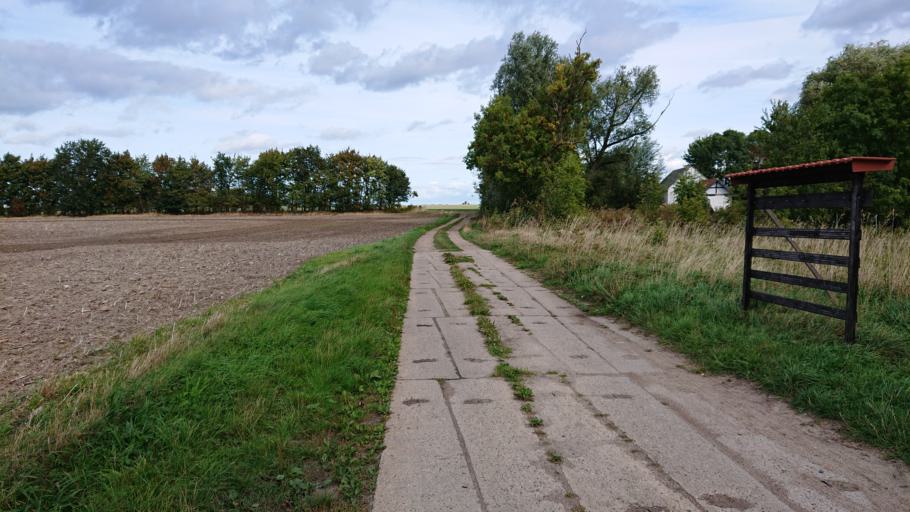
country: DE
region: Mecklenburg-Vorpommern
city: Altefahr
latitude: 54.3528
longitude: 13.1301
